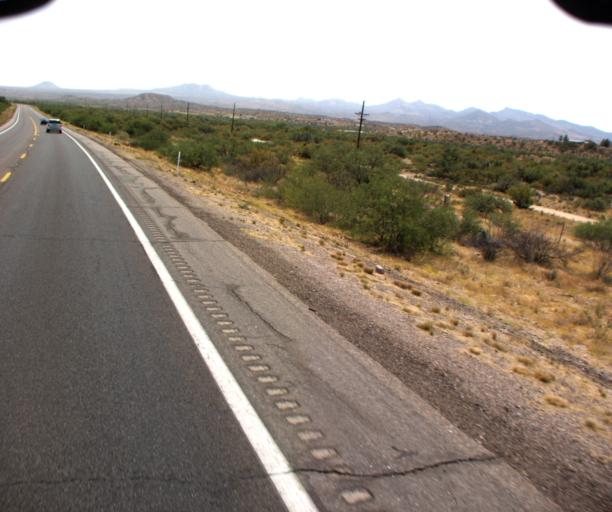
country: US
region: Arizona
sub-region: Gila County
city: Globe
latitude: 33.3621
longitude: -110.7058
